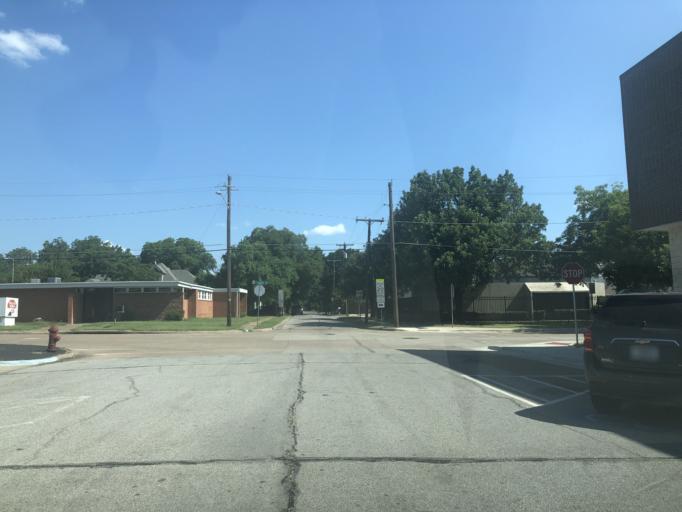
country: US
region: Texas
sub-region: Dallas County
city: Grand Prairie
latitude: 32.7465
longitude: -97.0020
